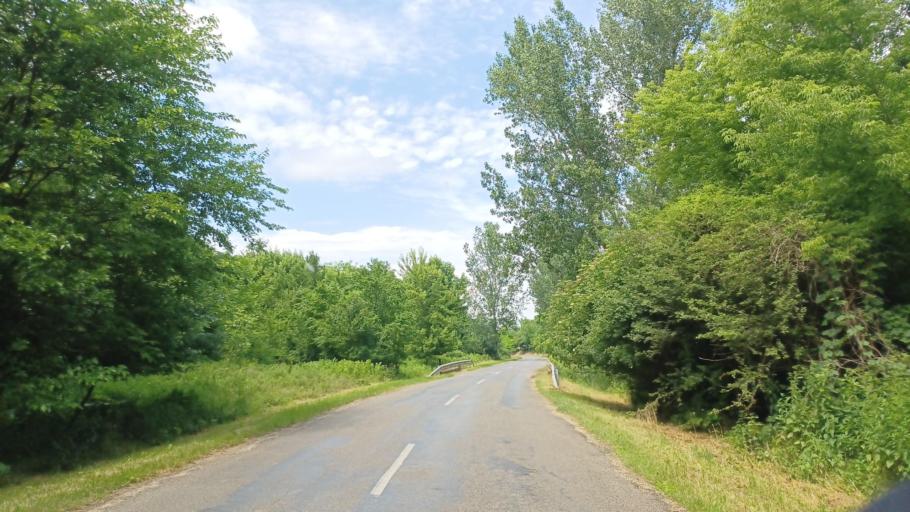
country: HU
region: Tolna
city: Simontornya
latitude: 46.7145
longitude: 18.5038
